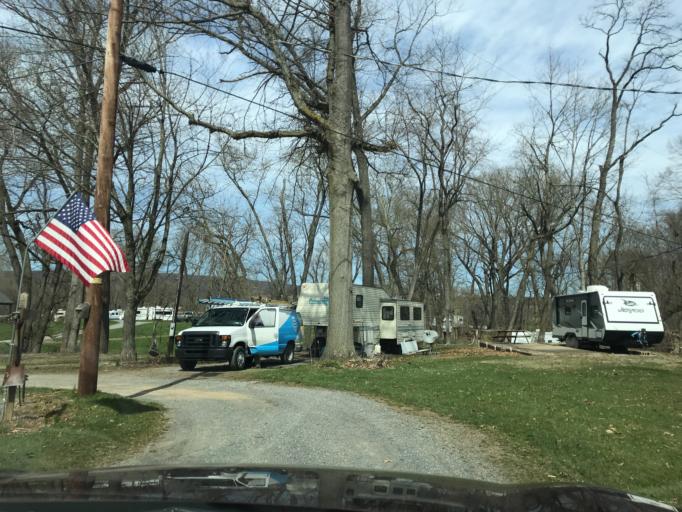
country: US
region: Pennsylvania
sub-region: Northumberland County
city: Northumberland
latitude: 40.9031
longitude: -76.8418
